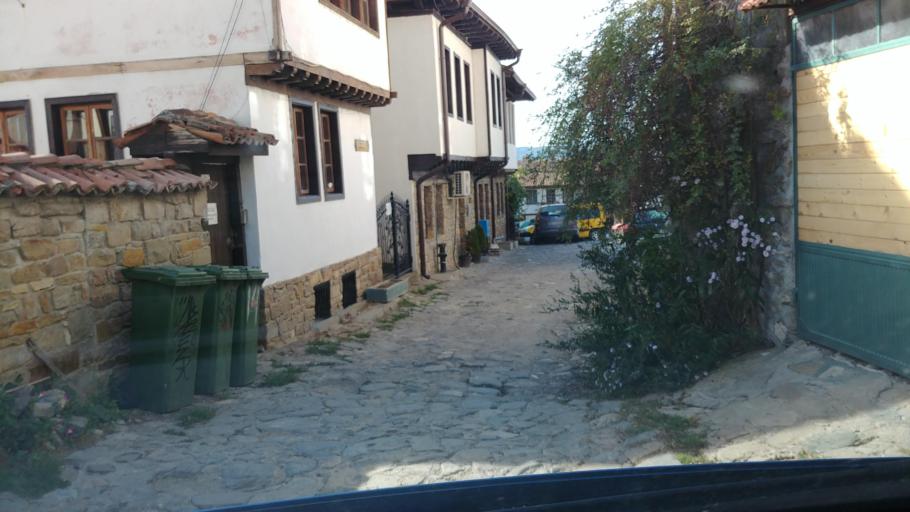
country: BG
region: Veliko Turnovo
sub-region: Obshtina Veliko Turnovo
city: Veliko Turnovo
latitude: 43.0846
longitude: 25.6401
